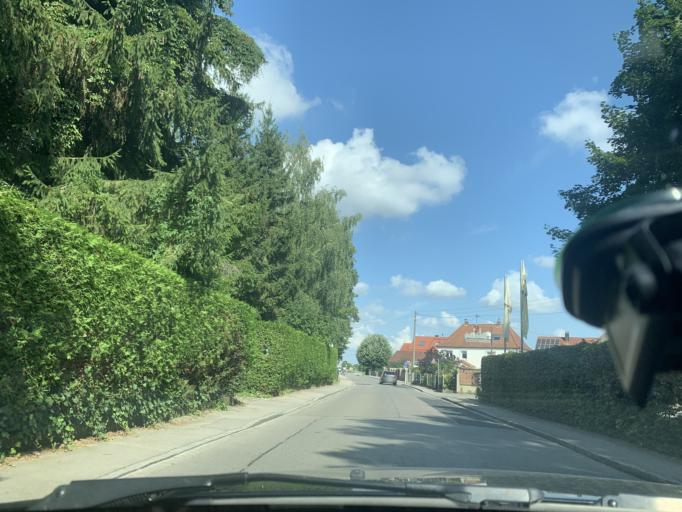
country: DE
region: Bavaria
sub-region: Swabia
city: Kissing
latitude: 48.3000
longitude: 10.9864
